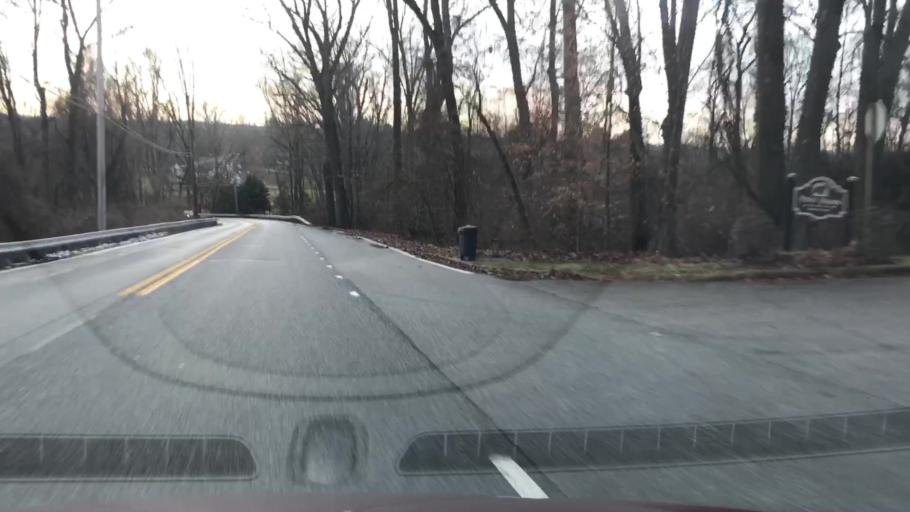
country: US
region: Maryland
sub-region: Baltimore County
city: Hunt Valley
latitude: 39.5838
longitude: -76.6306
